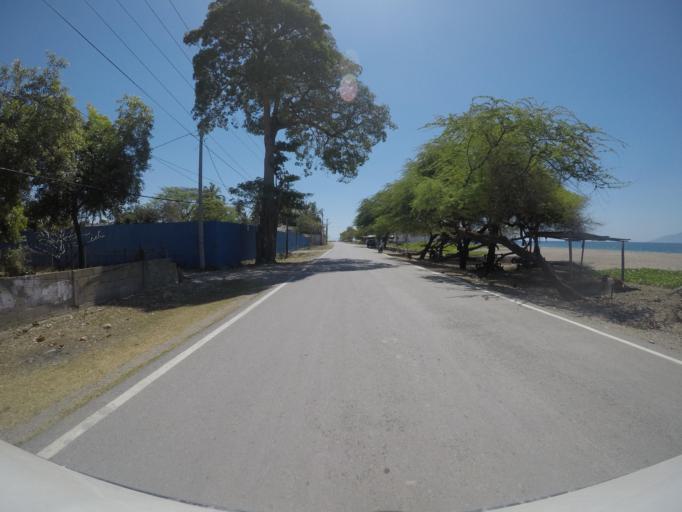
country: TL
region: Dili
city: Dili
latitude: -8.5395
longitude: 125.5375
